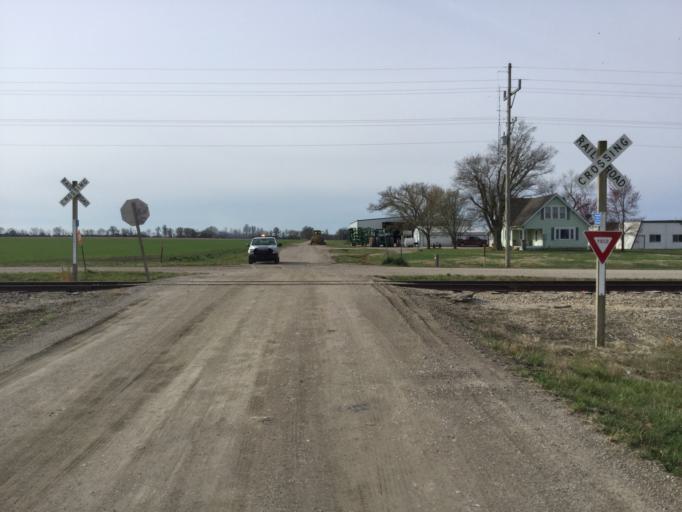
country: US
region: Kansas
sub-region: Cherokee County
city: Columbus
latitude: 37.1790
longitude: -94.9226
